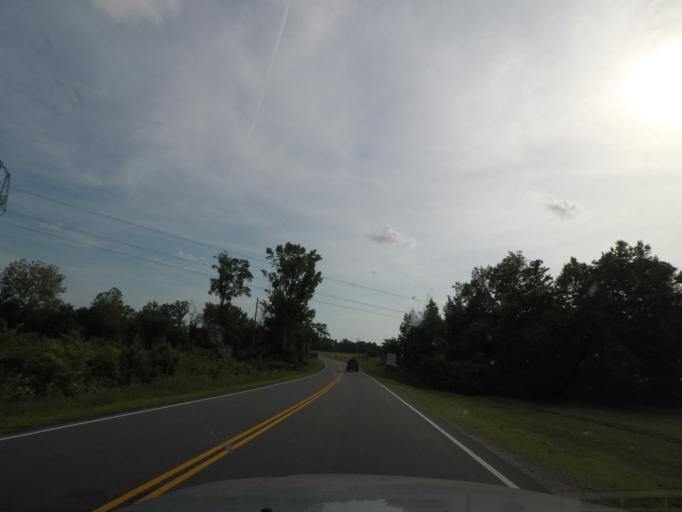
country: US
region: Virginia
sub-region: Mecklenburg County
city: Chase City
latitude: 36.8639
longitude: -78.5860
